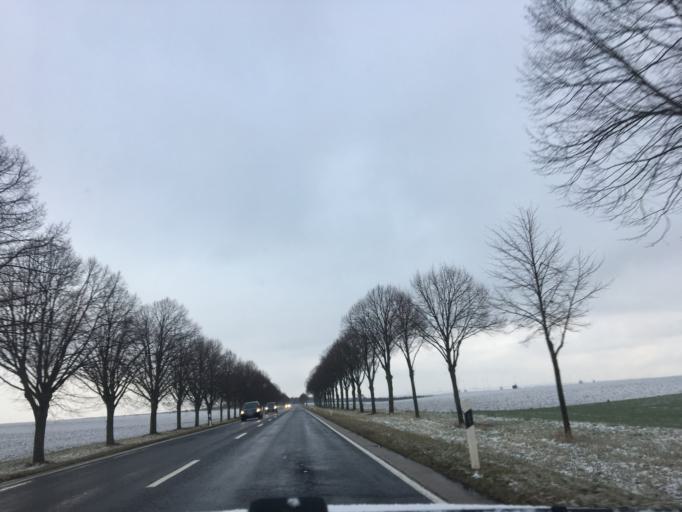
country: DE
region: Rheinland-Pfalz
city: Mauchenheim
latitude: 49.7093
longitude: 8.0582
